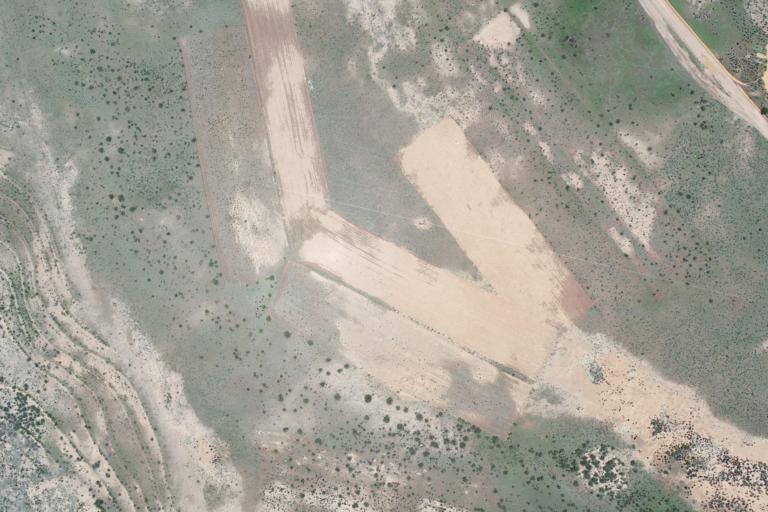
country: BO
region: La Paz
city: Curahuara de Carangas
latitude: -17.2861
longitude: -68.5087
